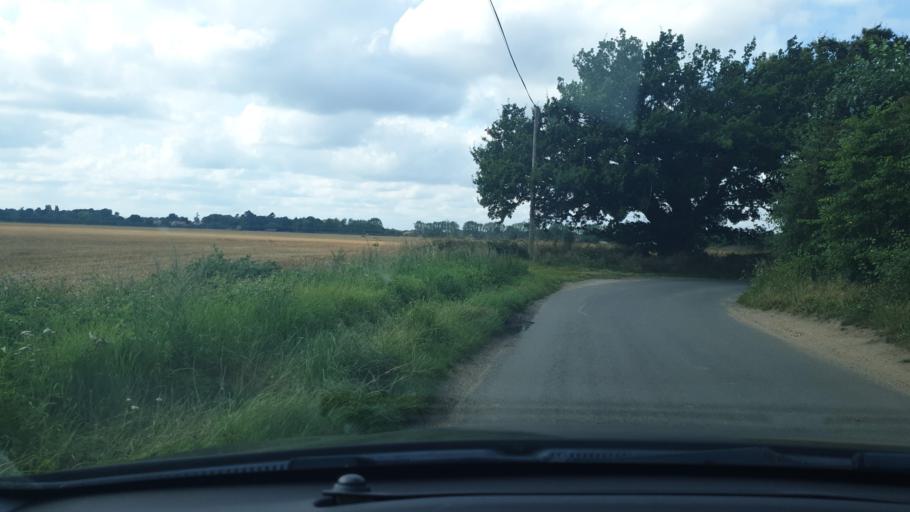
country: GB
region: England
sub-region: Suffolk
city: East Bergholt
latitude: 51.9225
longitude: 0.9996
